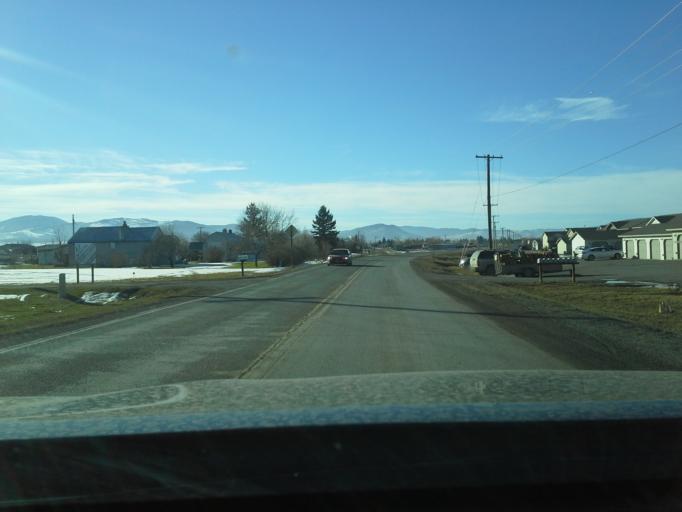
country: US
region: Montana
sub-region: Lewis and Clark County
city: East Helena
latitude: 46.5878
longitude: -111.8941
